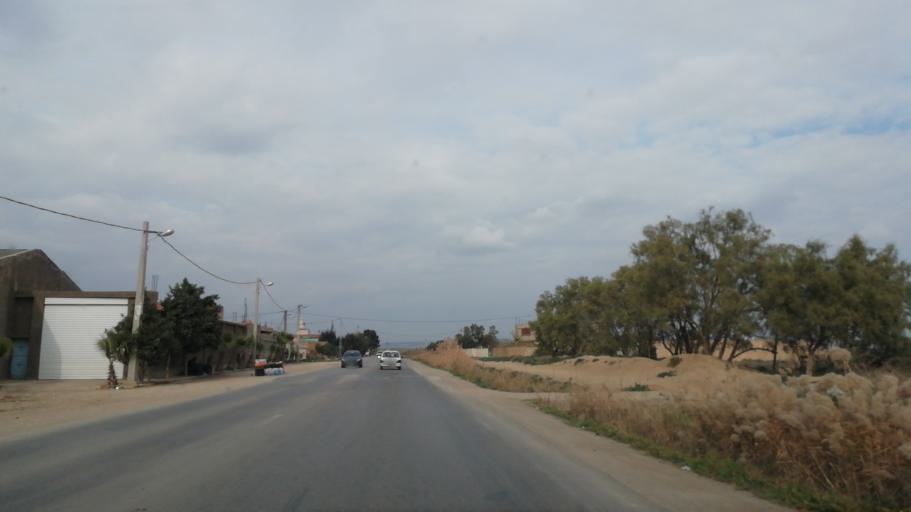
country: DZ
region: Mostaganem
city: Mostaganem
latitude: 35.6965
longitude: 0.0556
